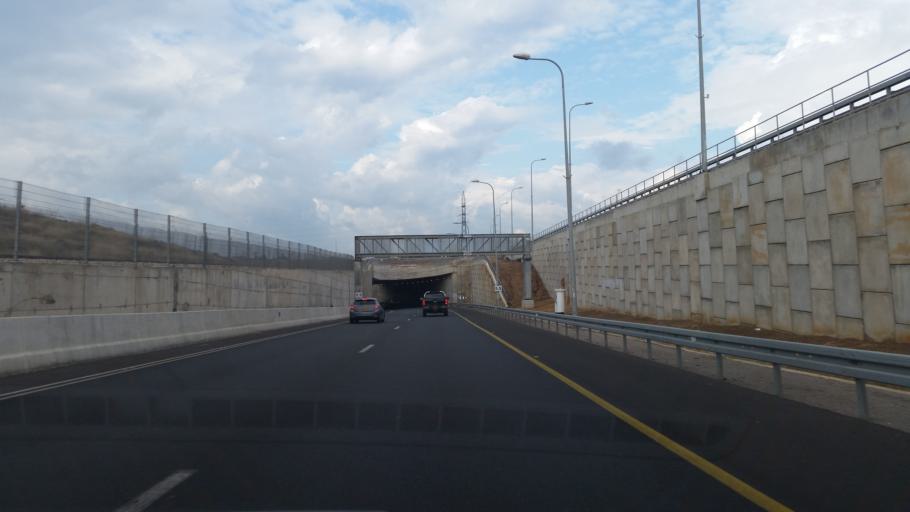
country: IL
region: Tel Aviv
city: Kefar Shemaryahu
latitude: 32.1932
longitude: 34.8352
